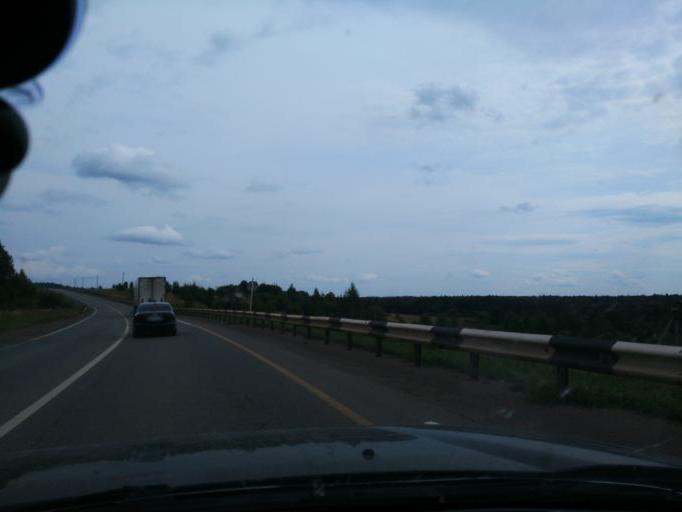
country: RU
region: Perm
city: Kuyeda
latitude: 56.4597
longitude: 55.6415
